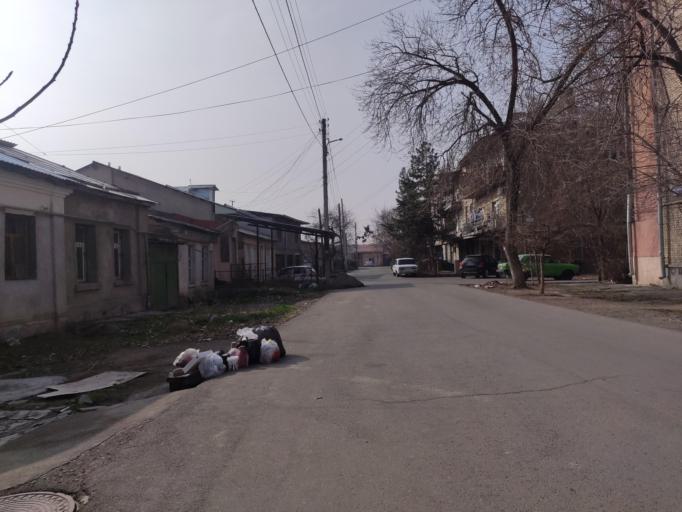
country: UZ
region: Toshkent Shahri
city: Tashkent
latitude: 41.2721
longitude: 69.2740
